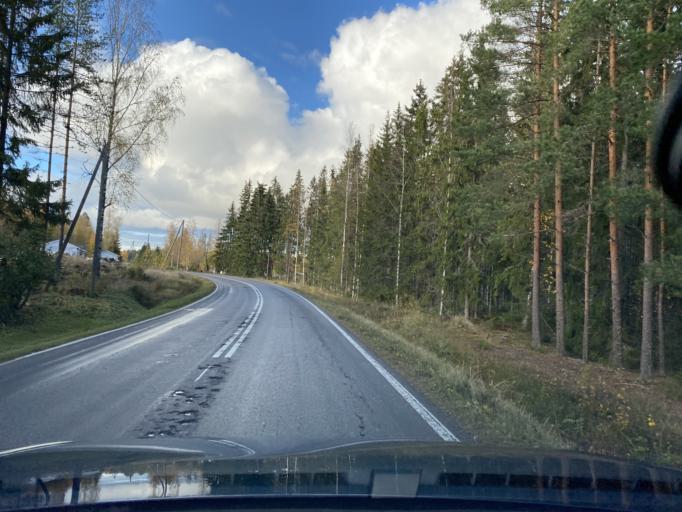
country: FI
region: Haeme
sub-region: Forssa
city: Humppila
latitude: 61.0173
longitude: 23.2515
